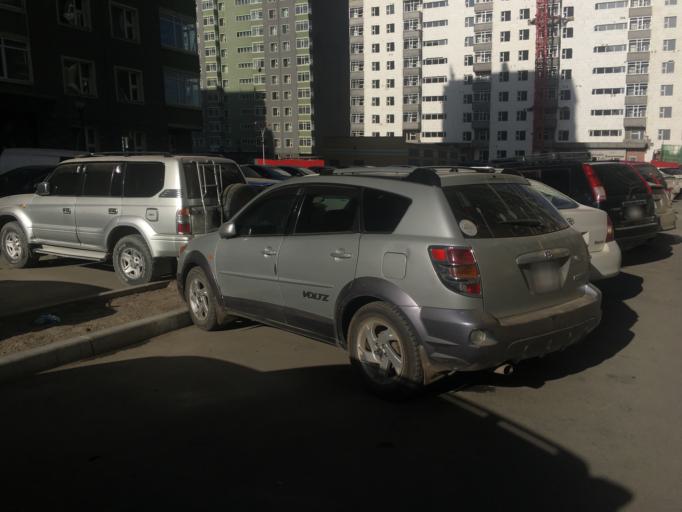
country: MN
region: Ulaanbaatar
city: Ulaanbaatar
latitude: 47.9205
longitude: 106.8197
